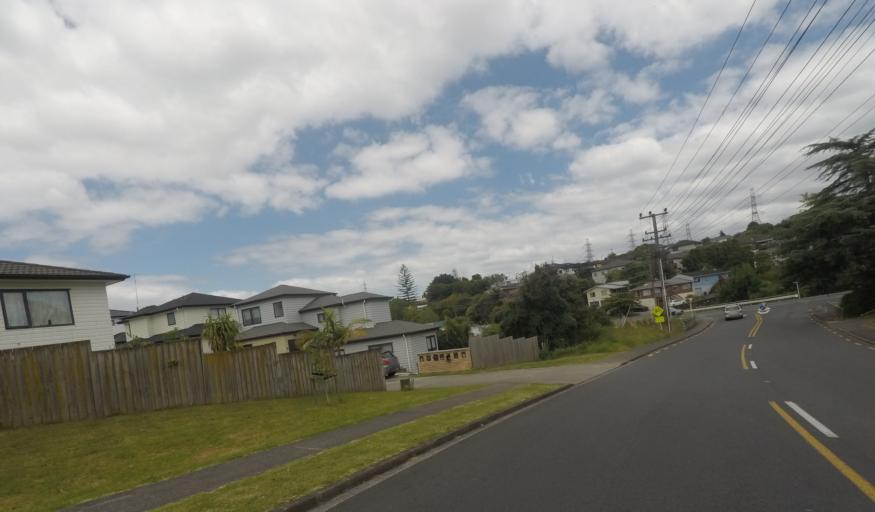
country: NZ
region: Auckland
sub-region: Auckland
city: Rosebank
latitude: -36.8369
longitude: 174.6178
